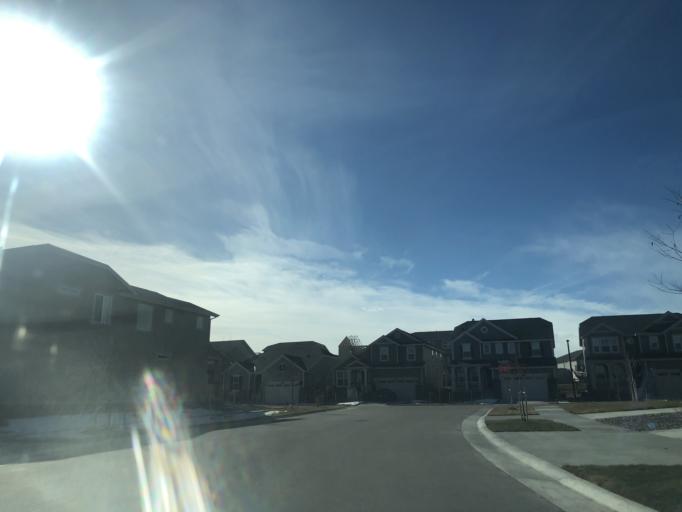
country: US
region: Colorado
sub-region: Douglas County
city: Stonegate
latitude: 39.5567
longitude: -104.8020
